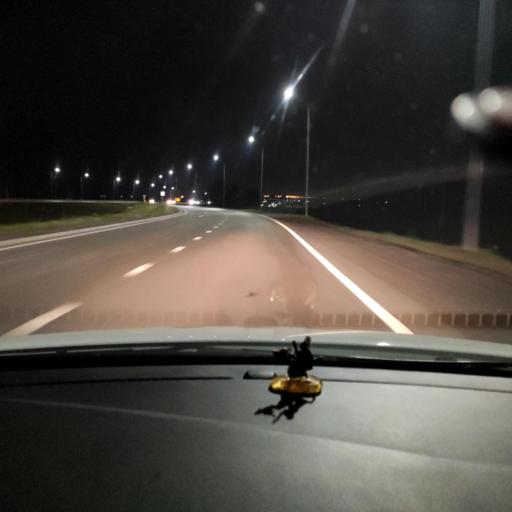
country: RU
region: Tatarstan
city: Vysokaya Gora
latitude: 55.8134
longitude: 49.4338
